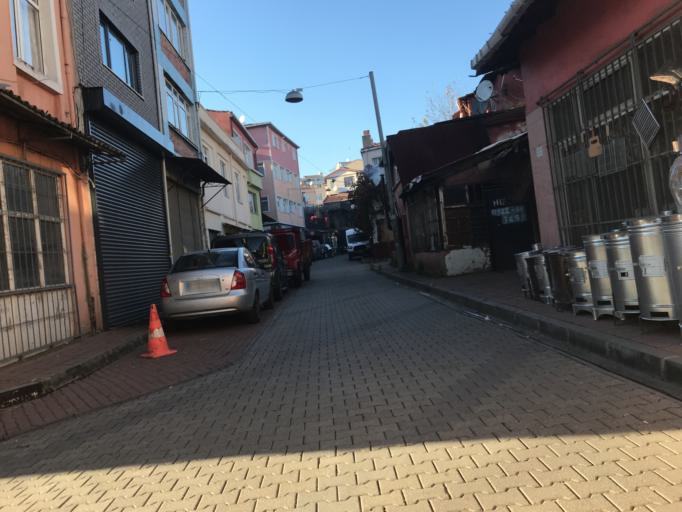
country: TR
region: Istanbul
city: Istanbul
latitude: 41.0245
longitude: 28.9586
